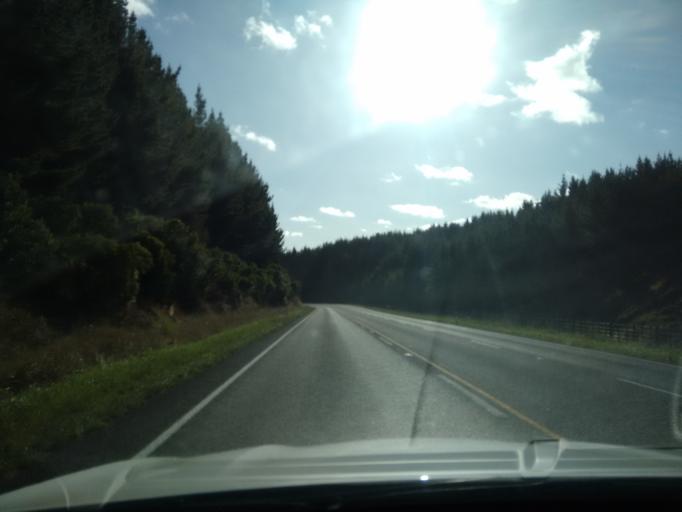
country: NZ
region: Manawatu-Wanganui
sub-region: Wanganui District
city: Wanganui
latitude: -39.8332
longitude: 174.9059
